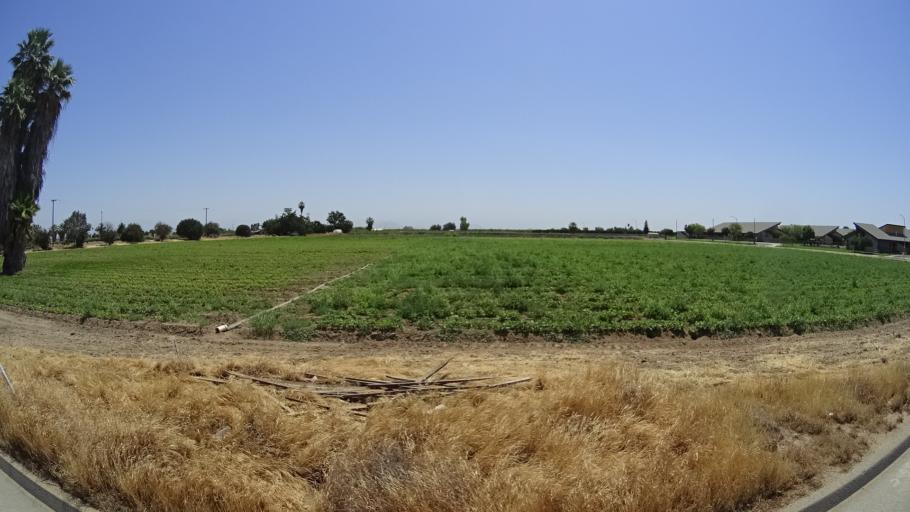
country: US
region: California
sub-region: Fresno County
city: Sunnyside
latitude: 36.7120
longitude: -119.6729
